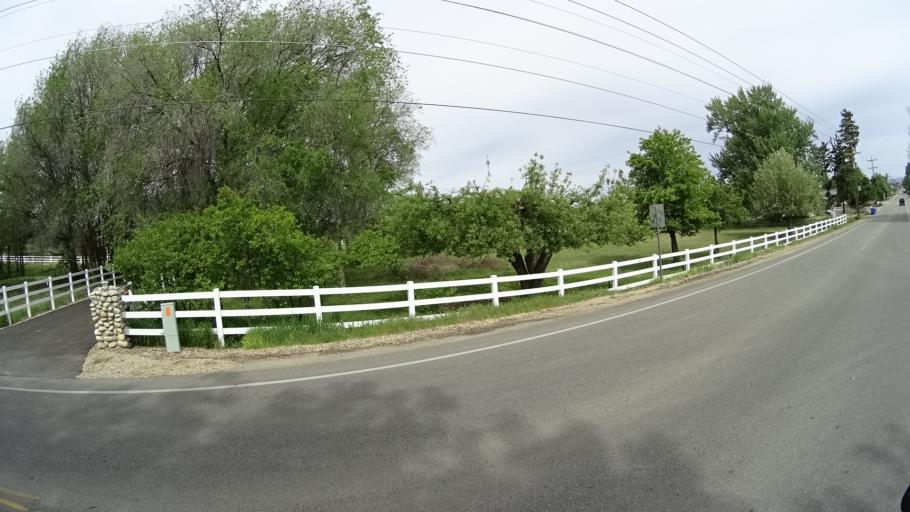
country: US
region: Idaho
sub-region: Ada County
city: Meridian
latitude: 43.5365
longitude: -116.3145
